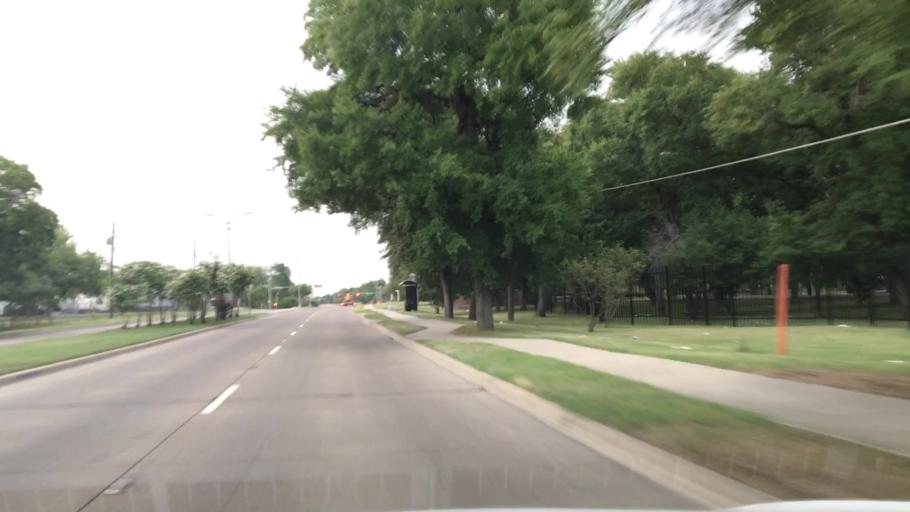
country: US
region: Texas
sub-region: Dallas County
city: Highland Park
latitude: 32.7931
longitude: -96.7150
